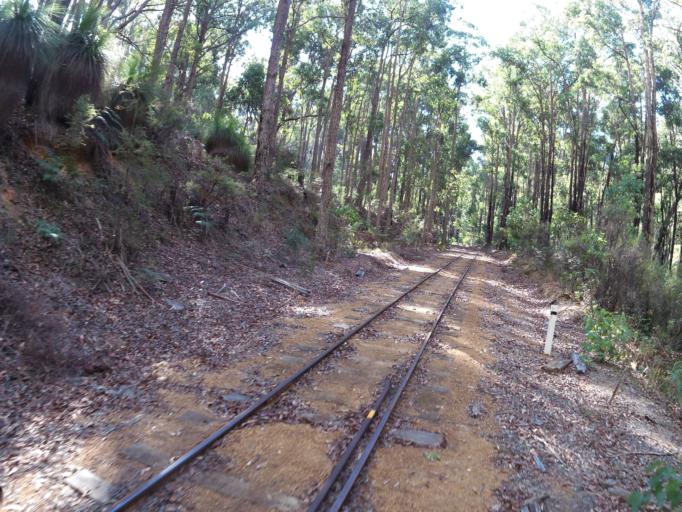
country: AU
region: Western Australia
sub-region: Waroona
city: Waroona
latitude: -32.7284
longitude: 116.1119
